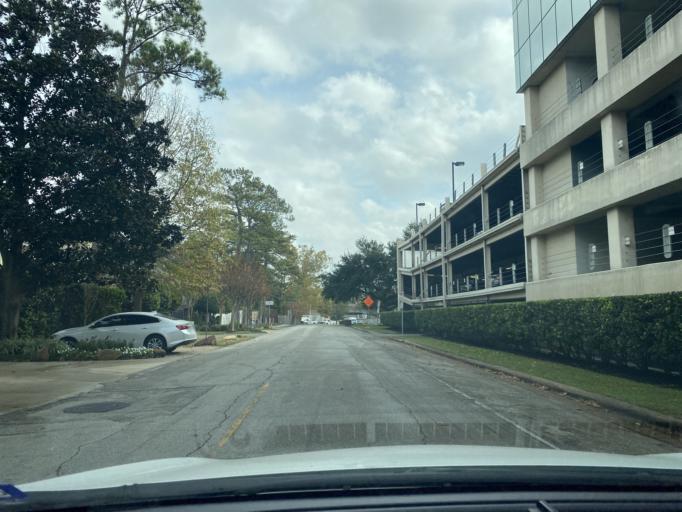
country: US
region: Texas
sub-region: Harris County
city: Hunters Creek Village
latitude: 29.7640
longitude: -95.4620
